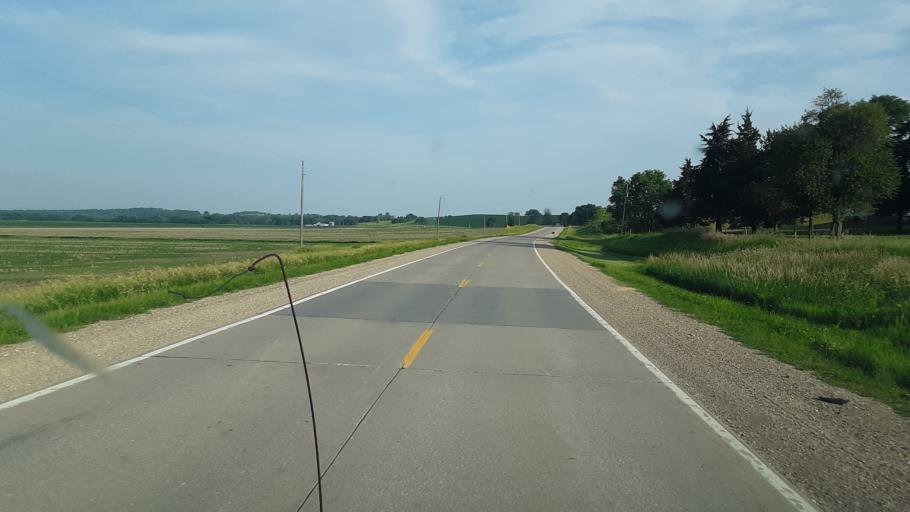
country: US
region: Iowa
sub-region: Tama County
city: Toledo
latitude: 41.9968
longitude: -92.7271
